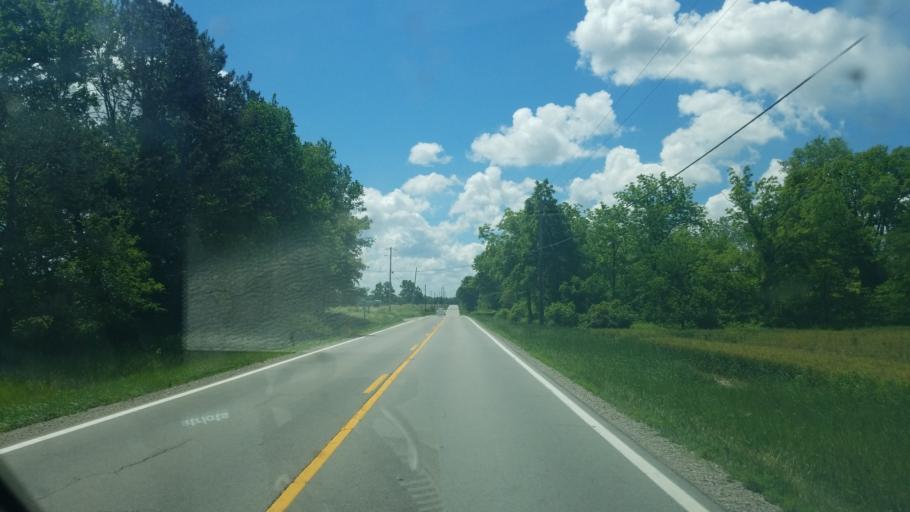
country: US
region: Ohio
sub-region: Huron County
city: New London
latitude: 41.1513
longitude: -82.4101
